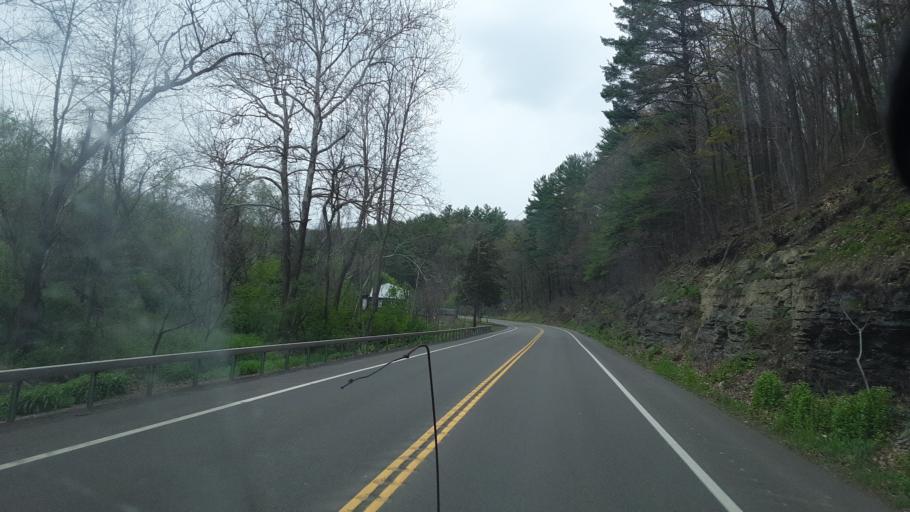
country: US
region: New York
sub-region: Steuben County
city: Addison
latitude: 42.0828
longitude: -77.2603
